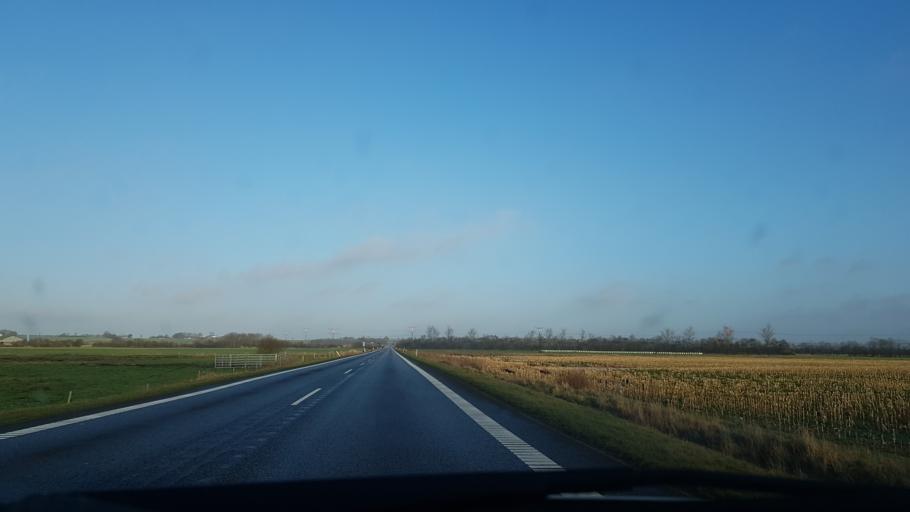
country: DK
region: South Denmark
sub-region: Tonder Kommune
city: Toftlund
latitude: 55.2372
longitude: 9.1271
